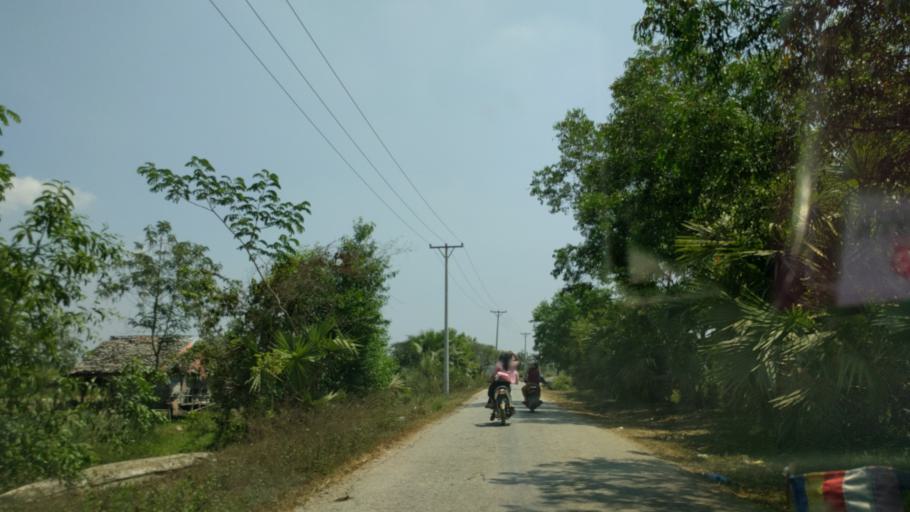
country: MM
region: Mon
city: Martaban
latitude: 16.5855
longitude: 97.6625
